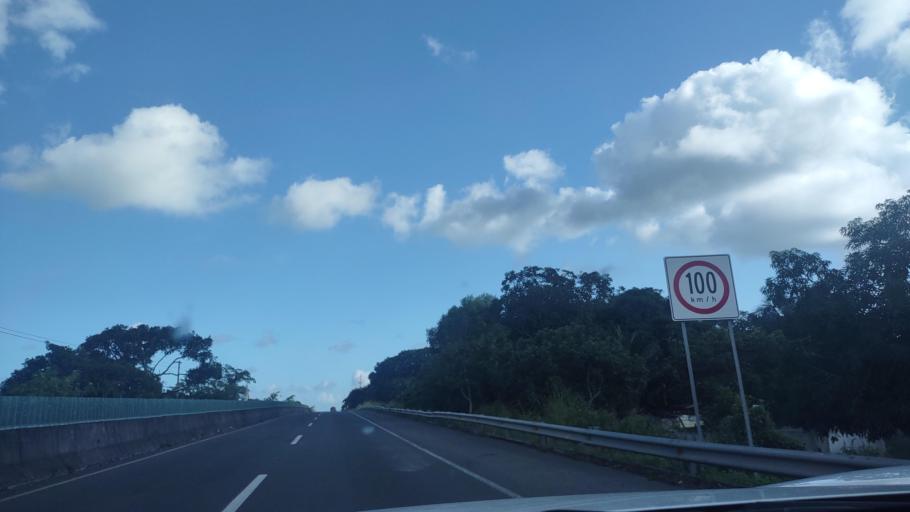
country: MX
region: Veracruz
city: El Tejar
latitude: 19.0603
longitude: -96.1720
